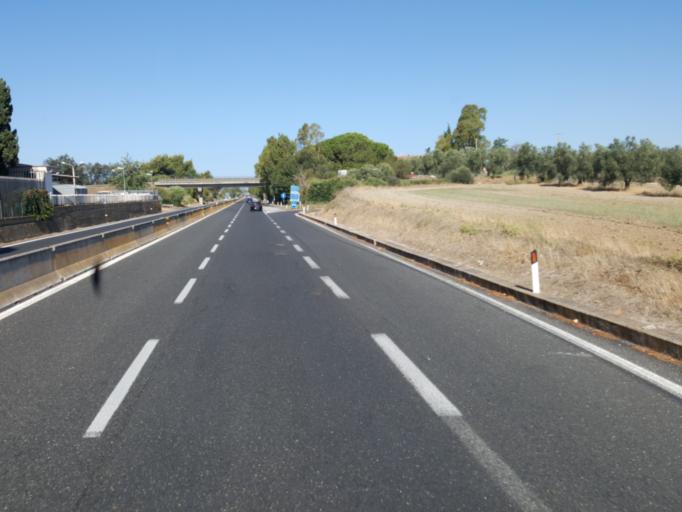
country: IT
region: Latium
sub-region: Provincia di Viterbo
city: Pescia Romana
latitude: 42.4020
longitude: 11.5011
